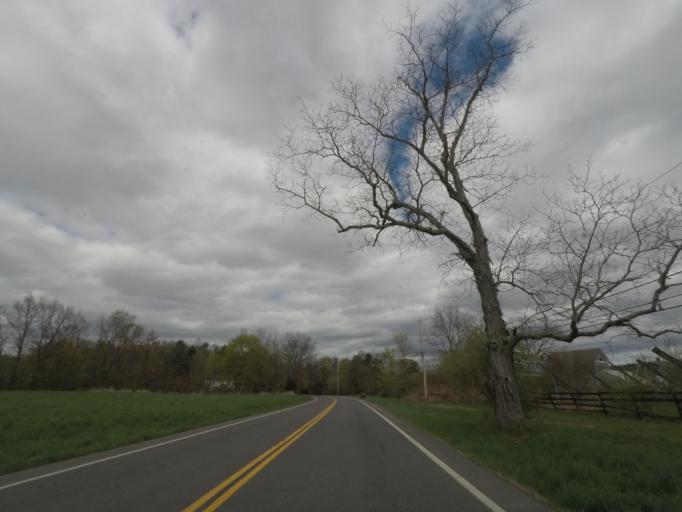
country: US
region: New York
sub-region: Columbia County
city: Philmont
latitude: 42.2992
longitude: -73.6370
